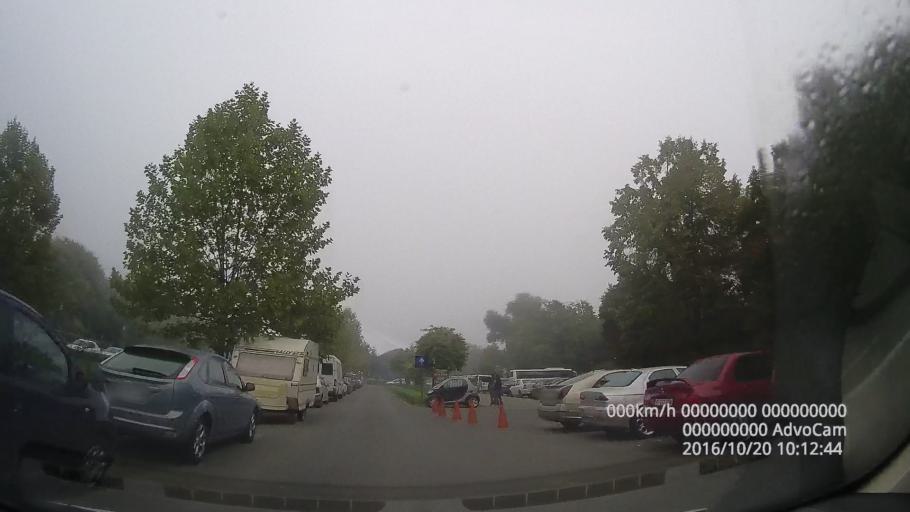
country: RO
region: Bucuresti
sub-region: Municipiul Bucuresti
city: Bucharest
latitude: 44.4564
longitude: 26.1069
